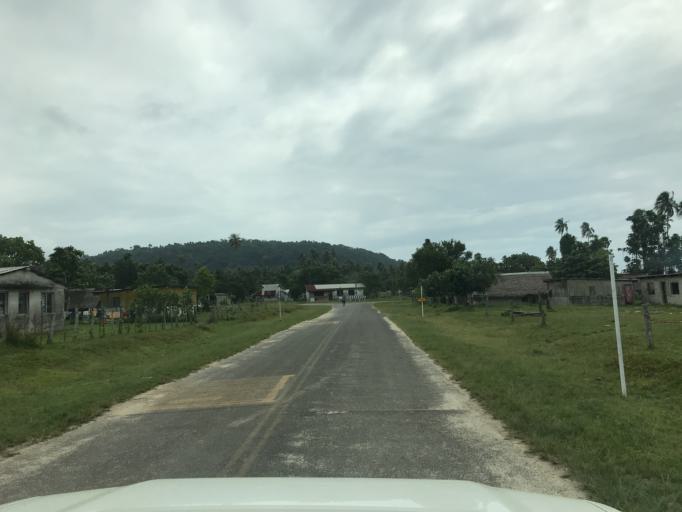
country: VU
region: Sanma
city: Port-Olry
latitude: -15.0431
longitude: 167.0721
